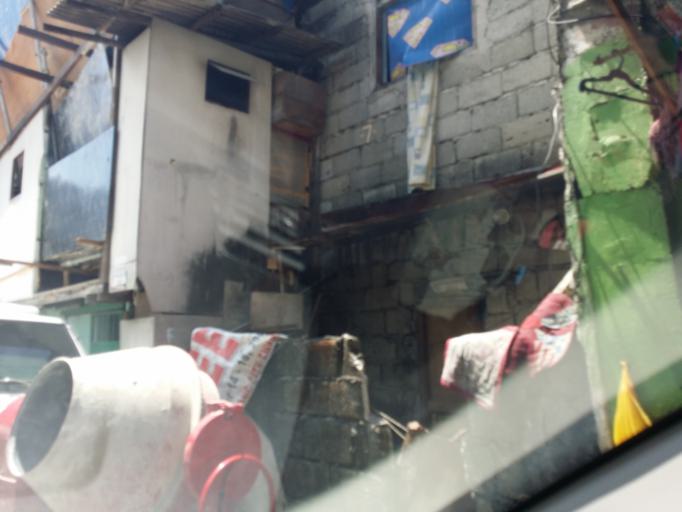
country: PH
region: Metro Manila
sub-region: Mandaluyong
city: Mandaluyong City
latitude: 14.5742
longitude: 121.0293
